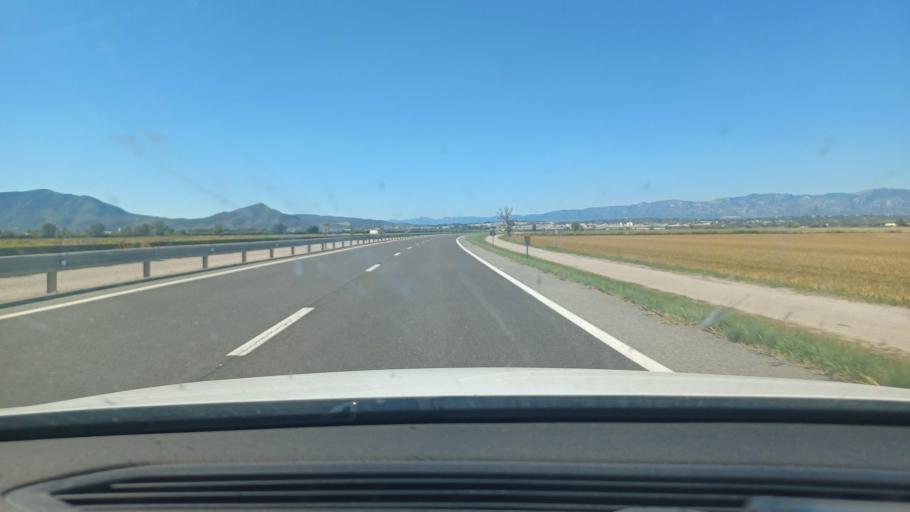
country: ES
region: Catalonia
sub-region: Provincia de Tarragona
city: Amposta
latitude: 40.7133
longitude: 0.6209
